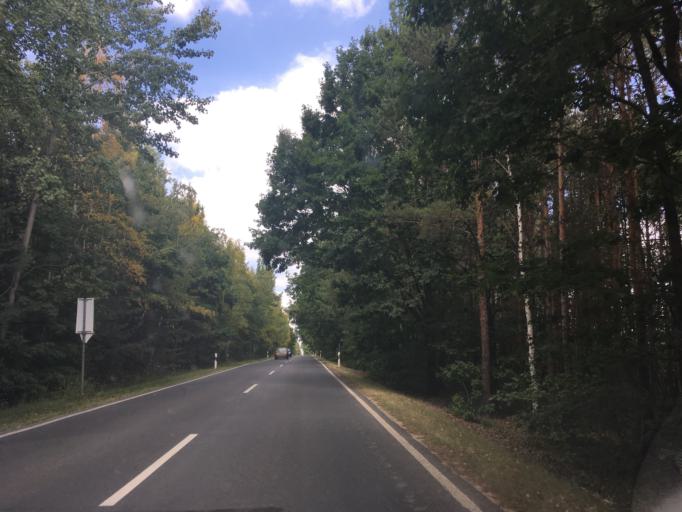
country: DE
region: Saxony
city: Ottendorf-Okrilla
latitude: 51.2030
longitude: 13.8269
